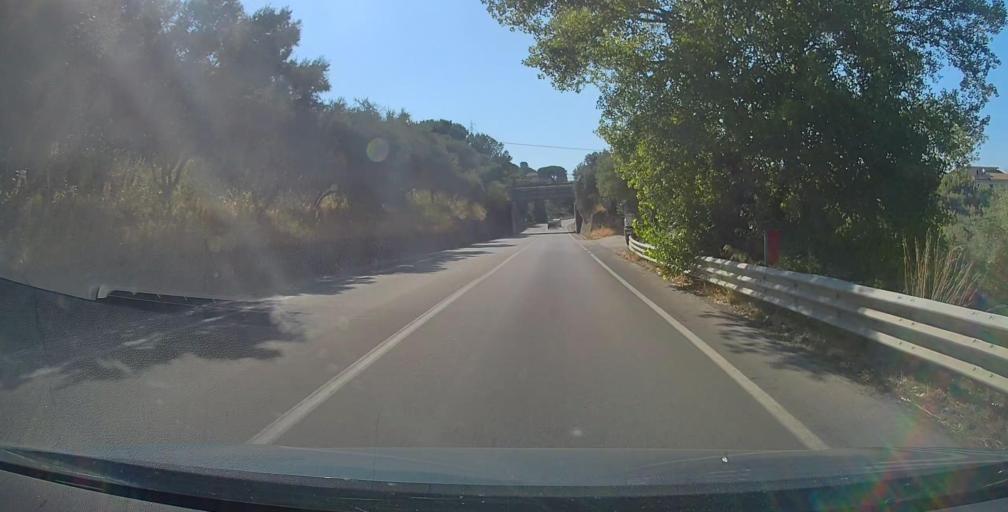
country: IT
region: Sicily
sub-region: Messina
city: Capo d'Orlando
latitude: 38.1519
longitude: 14.7647
